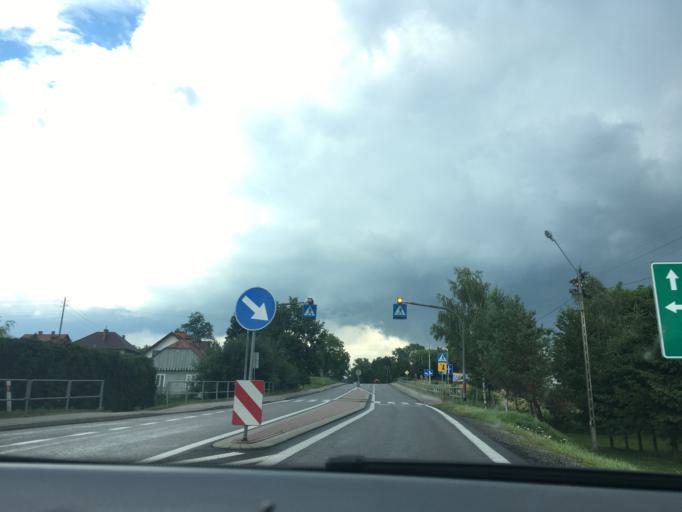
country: PL
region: Subcarpathian Voivodeship
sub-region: Powiat brzozowski
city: Jablonica Polska
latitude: 49.7050
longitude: 21.8875
